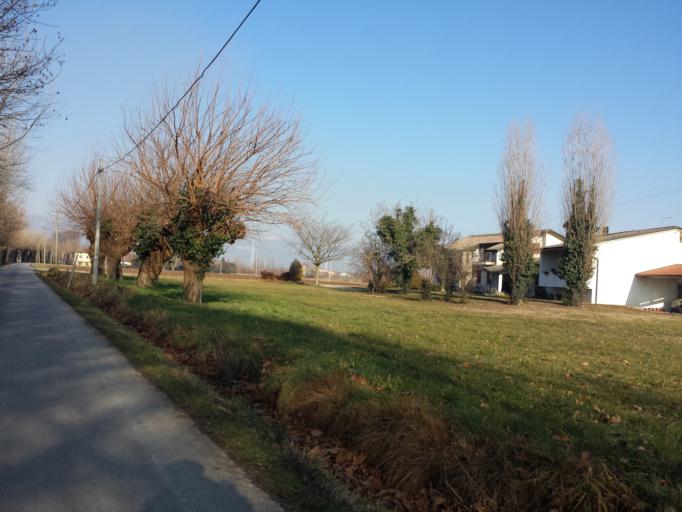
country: IT
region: Veneto
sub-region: Provincia di Vicenza
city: Sandrigo
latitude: 45.6413
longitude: 11.6028
